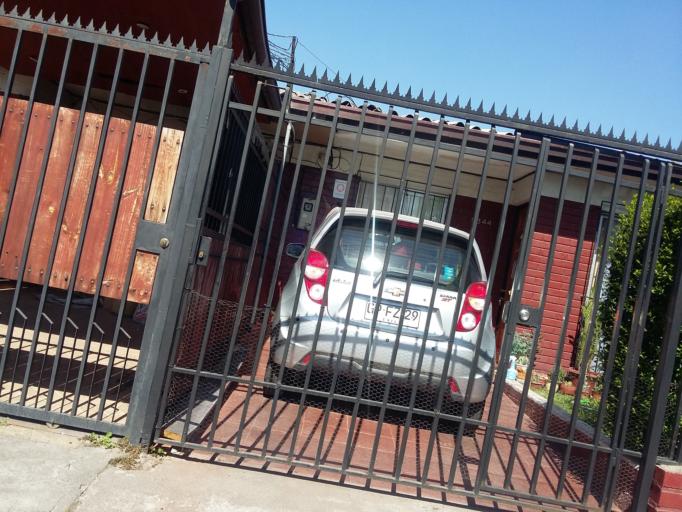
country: CL
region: Santiago Metropolitan
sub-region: Provincia de Santiago
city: La Pintana
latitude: -33.5403
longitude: -70.5815
